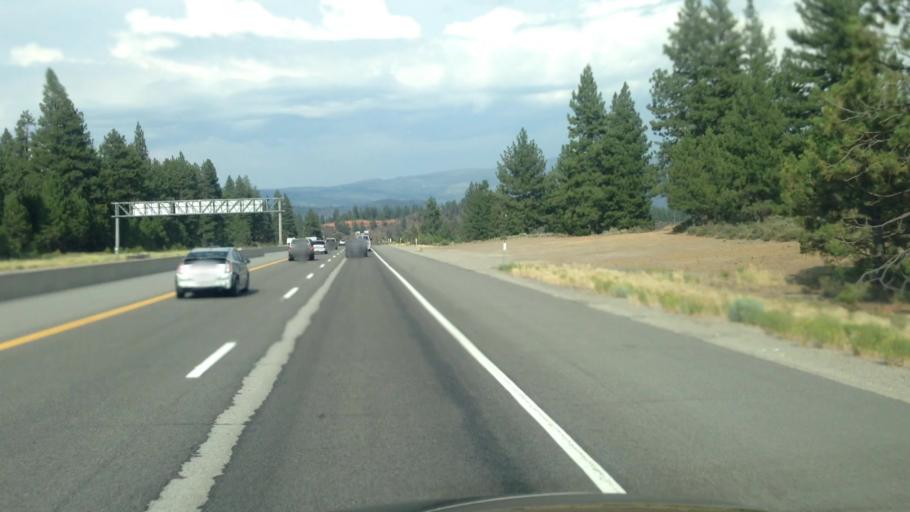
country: US
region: California
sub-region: Nevada County
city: Truckee
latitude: 39.3622
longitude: -120.1283
